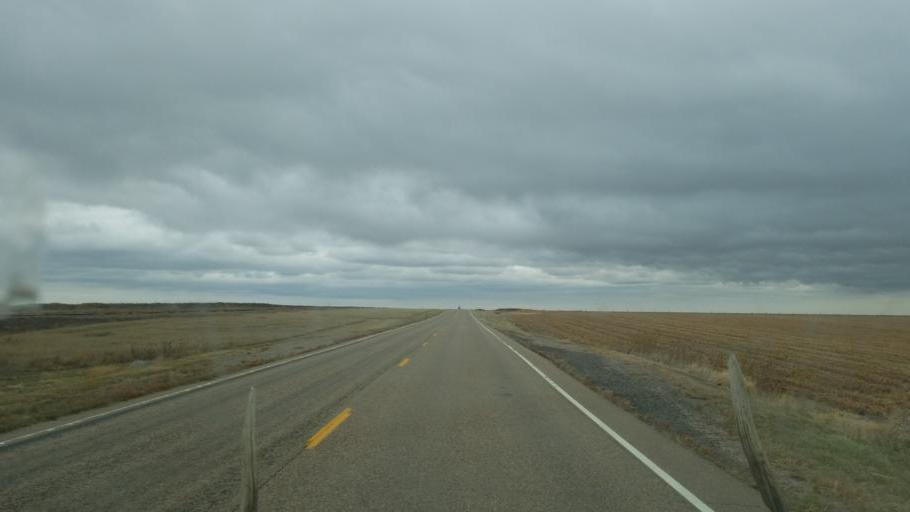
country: US
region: Colorado
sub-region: Cheyenne County
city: Cheyenne Wells
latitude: 38.8167
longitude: -102.5229
